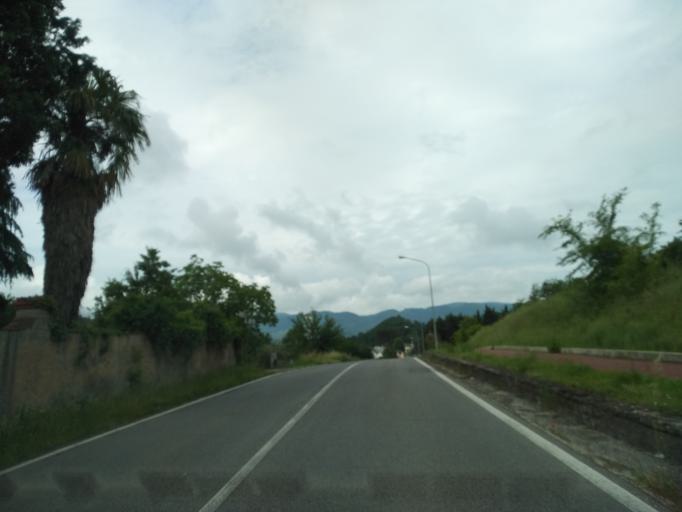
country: IT
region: Tuscany
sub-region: Province of Arezzo
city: Vacchereccia
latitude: 43.5747
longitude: 11.4979
